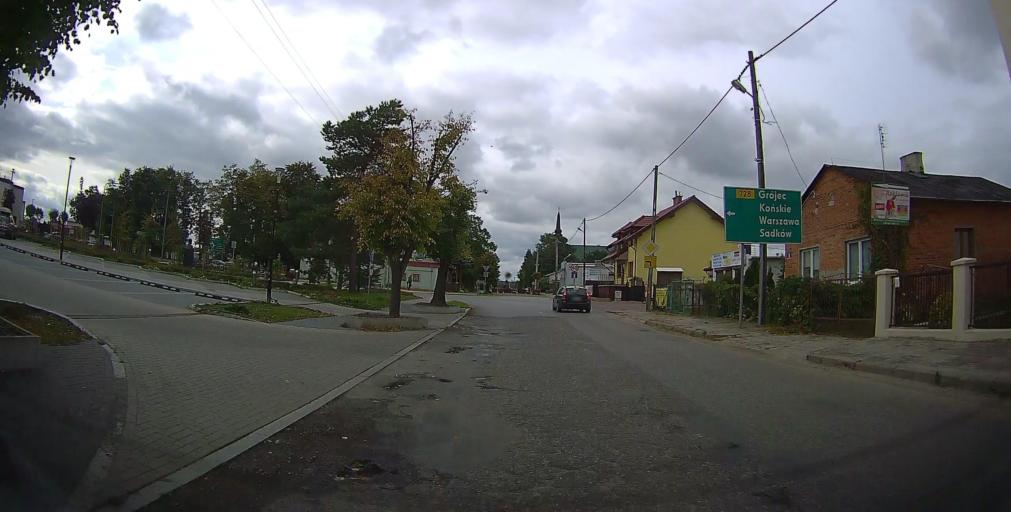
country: PL
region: Masovian Voivodeship
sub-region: Powiat grojecki
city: Belsk Duzy
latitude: 51.8251
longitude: 20.8109
